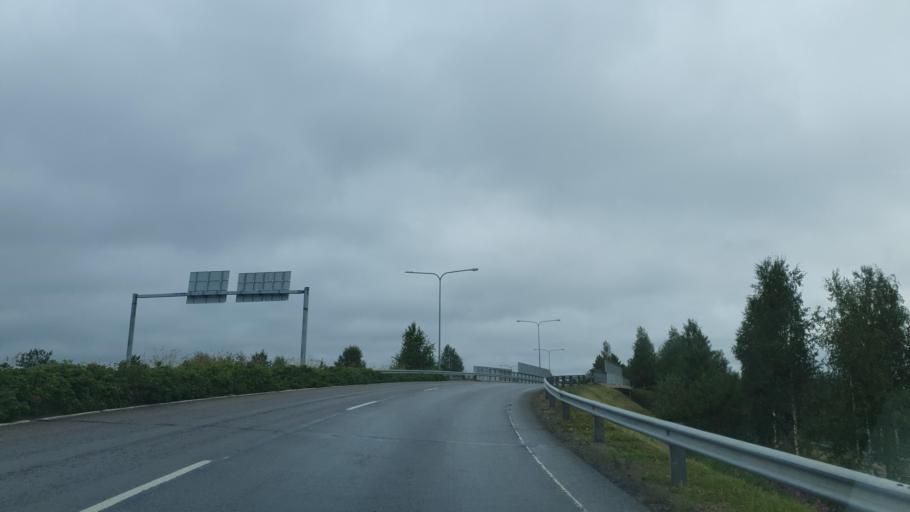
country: FI
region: Lapland
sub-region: Itae-Lappi
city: Kemijaervi
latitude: 66.7171
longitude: 27.4242
